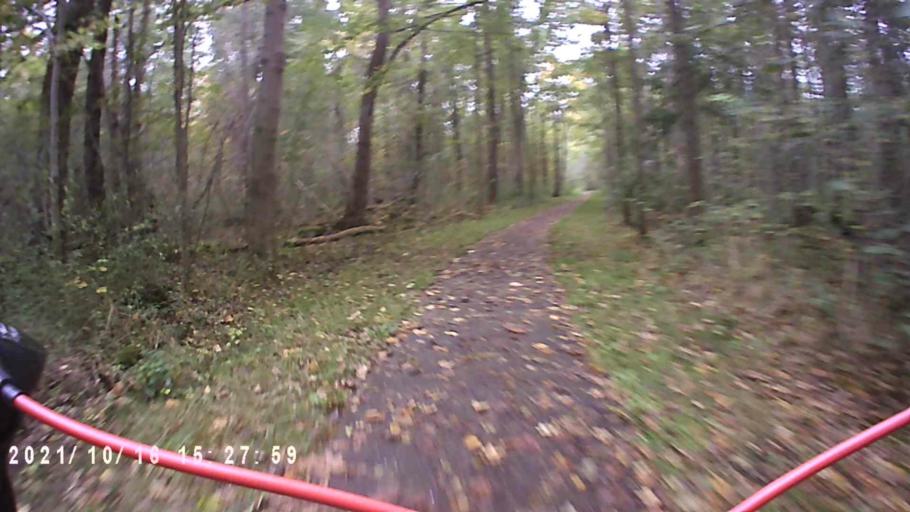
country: NL
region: Friesland
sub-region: Gemeente Dongeradeel
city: Anjum
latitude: 53.4041
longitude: 6.2266
